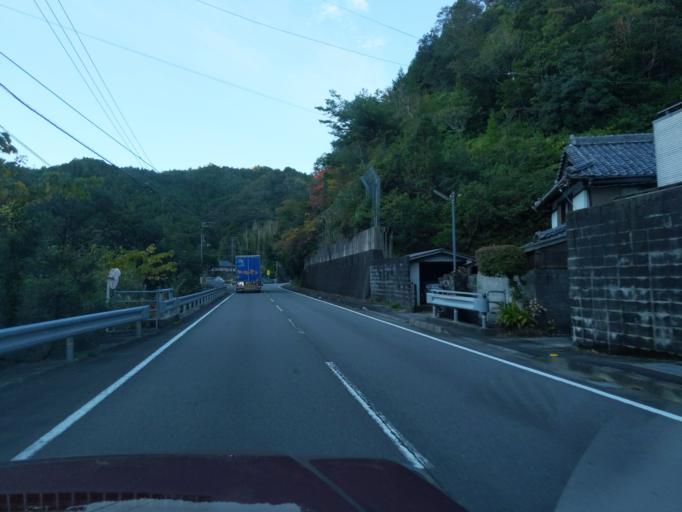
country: JP
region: Tokushima
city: Anan
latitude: 33.7141
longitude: 134.4813
